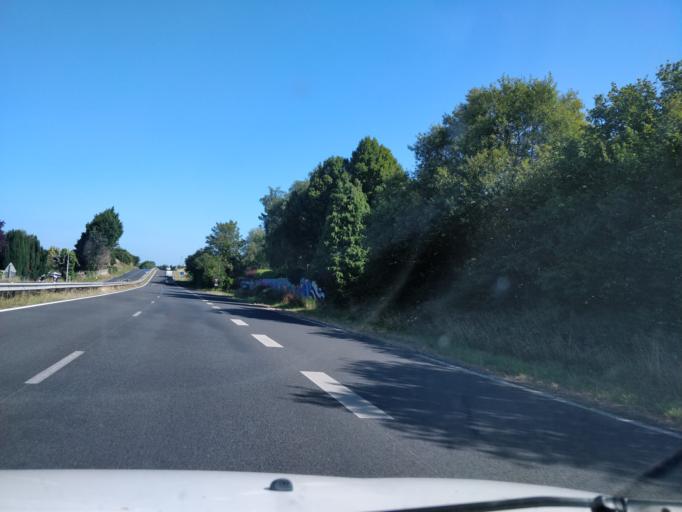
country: FR
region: Brittany
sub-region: Departement des Cotes-d'Armor
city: Pordic
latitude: 48.5745
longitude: -2.8230
